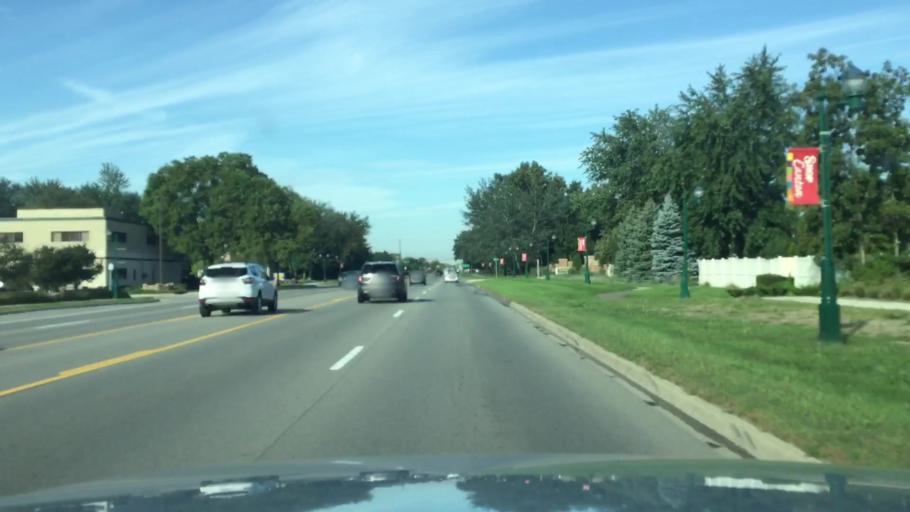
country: US
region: Michigan
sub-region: Wayne County
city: Canton
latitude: 42.3225
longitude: -83.4632
